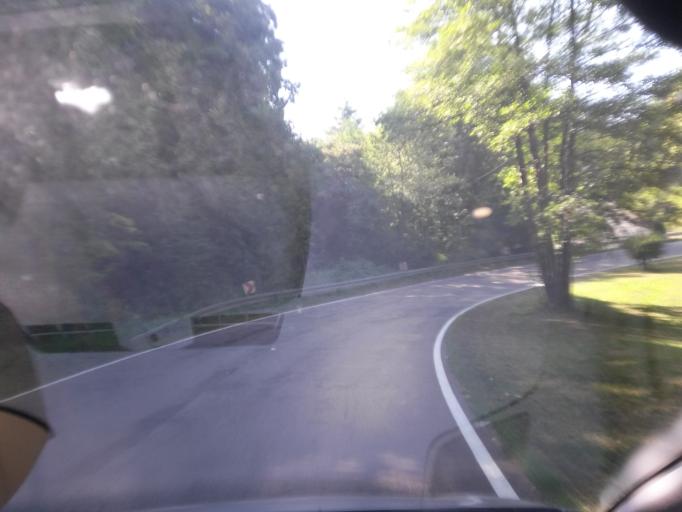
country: DE
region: Saarland
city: Orscholz
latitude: 49.4862
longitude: 6.5222
